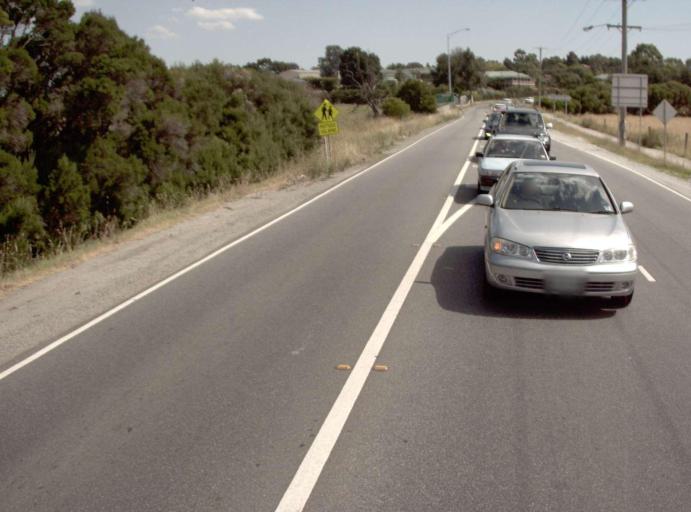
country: AU
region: Victoria
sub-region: Casey
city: Narre Warren
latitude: -38.0293
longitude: 145.3005
